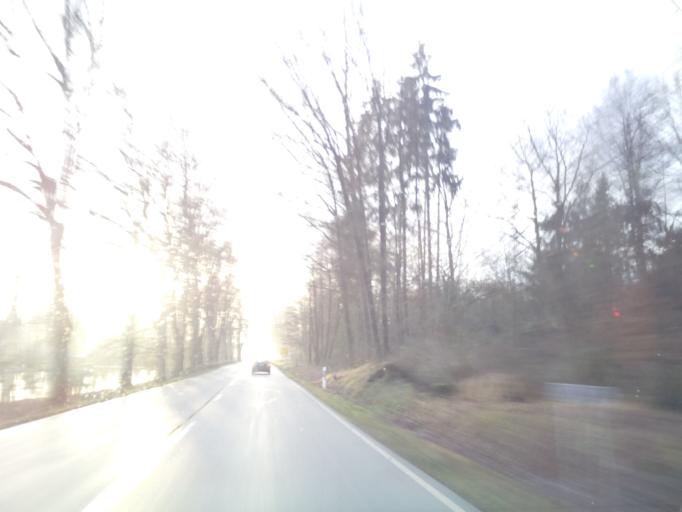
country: DE
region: Bavaria
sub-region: Upper Franconia
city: Lichtenfels
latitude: 50.1626
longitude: 11.0550
